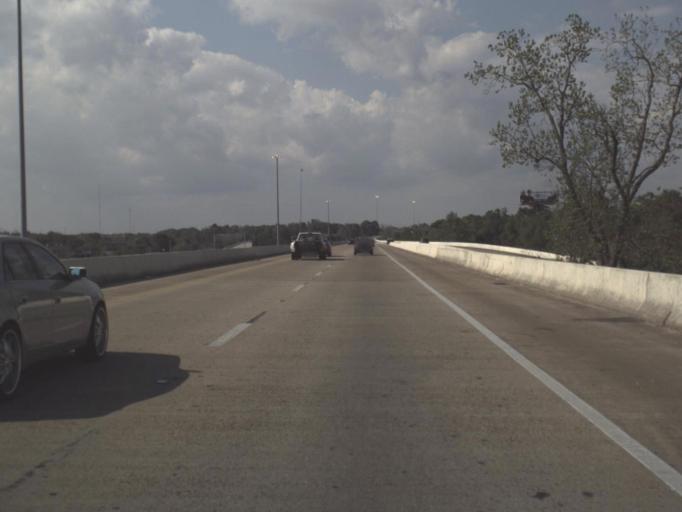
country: US
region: Florida
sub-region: Escambia County
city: Pensacola
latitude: 30.4238
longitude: -87.2143
